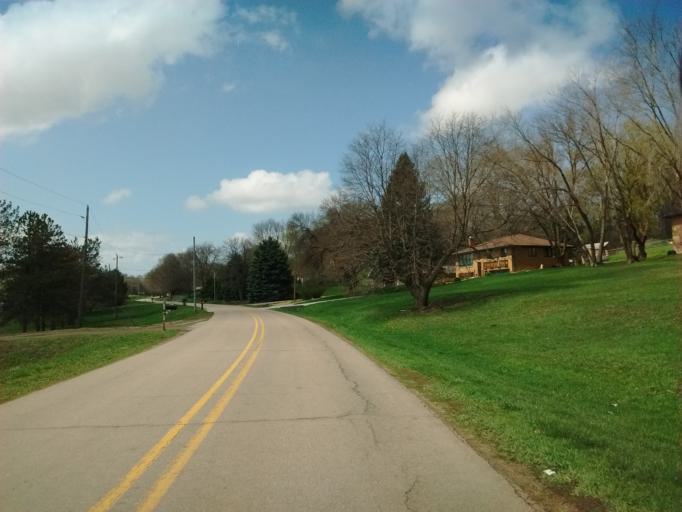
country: US
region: South Dakota
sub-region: Union County
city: North Sioux City
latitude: 42.5520
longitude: -96.4431
